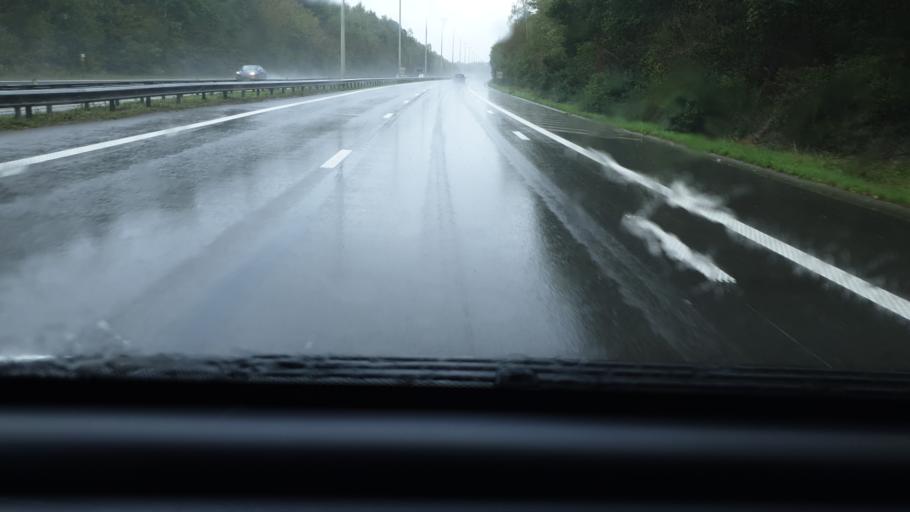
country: BE
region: Wallonia
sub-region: Province du Hainaut
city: Farciennes
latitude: 50.4452
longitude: 4.4971
